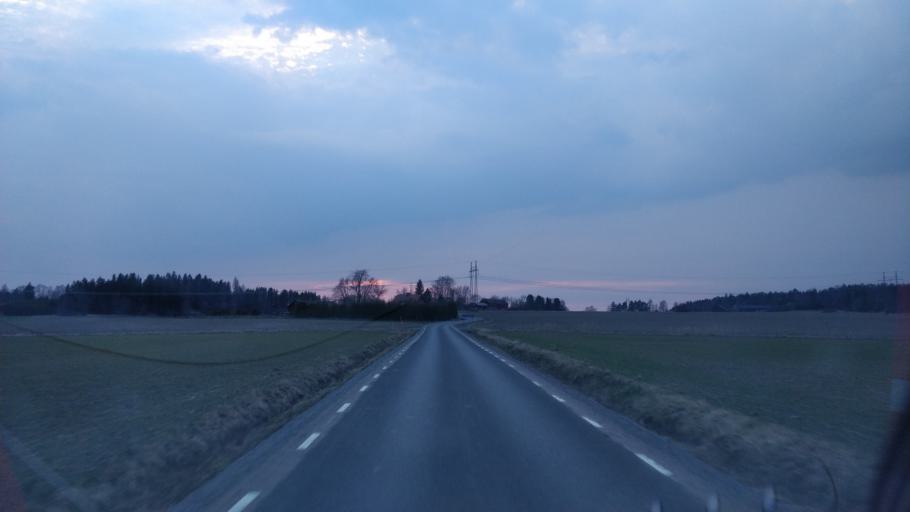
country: SE
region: Uppsala
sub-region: Enkopings Kommun
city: Orsundsbro
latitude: 59.7205
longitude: 17.2366
